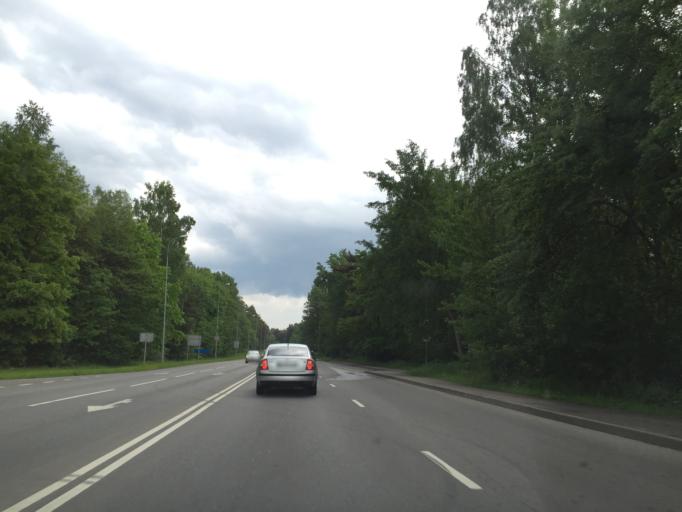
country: LT
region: Klaipedos apskritis
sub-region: Klaipeda
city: Klaipeda
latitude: 55.7373
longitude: 21.0961
